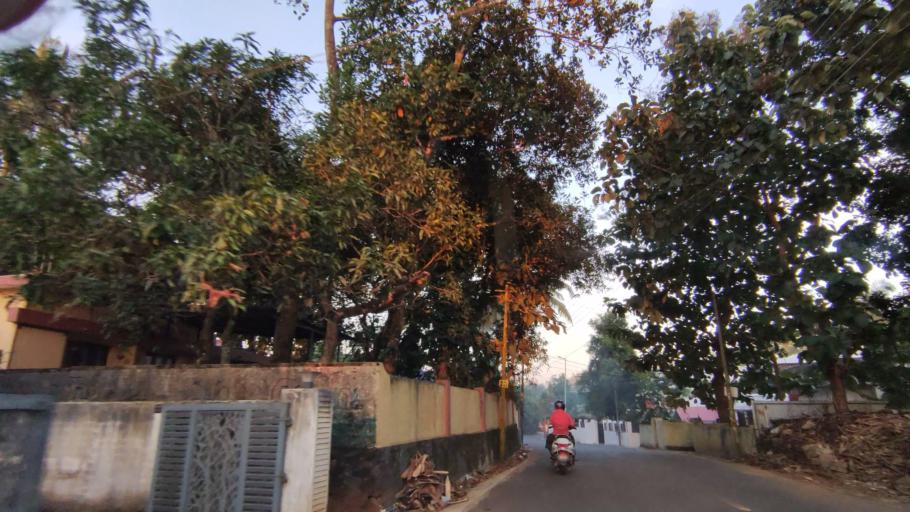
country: IN
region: Kerala
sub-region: Kottayam
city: Kottayam
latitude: 9.6420
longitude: 76.5037
